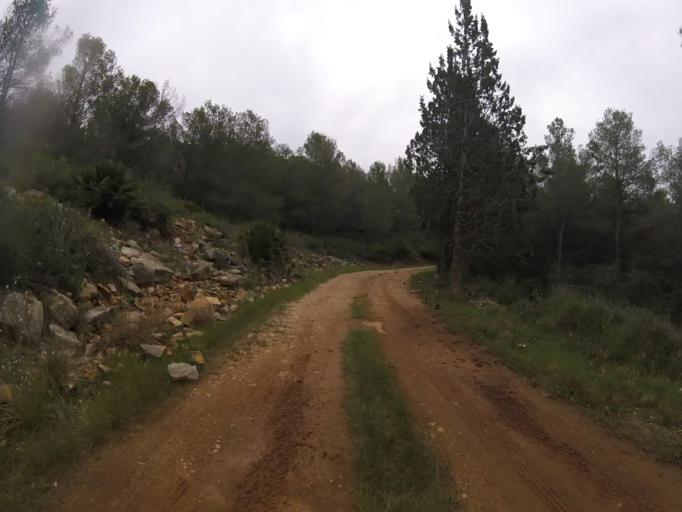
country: ES
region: Valencia
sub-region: Provincia de Castello
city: Santa Magdalena de Pulpis
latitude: 40.3191
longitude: 0.2777
